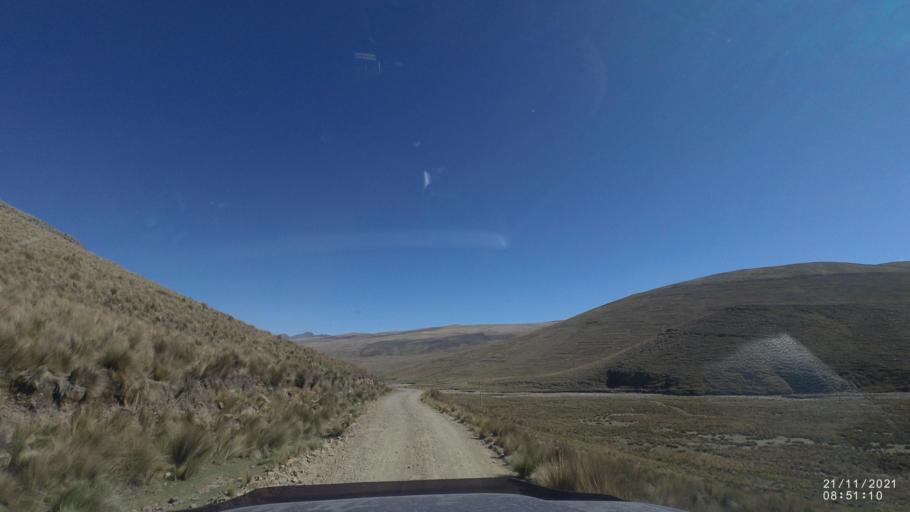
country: BO
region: Cochabamba
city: Cochabamba
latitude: -17.2205
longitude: -66.2367
